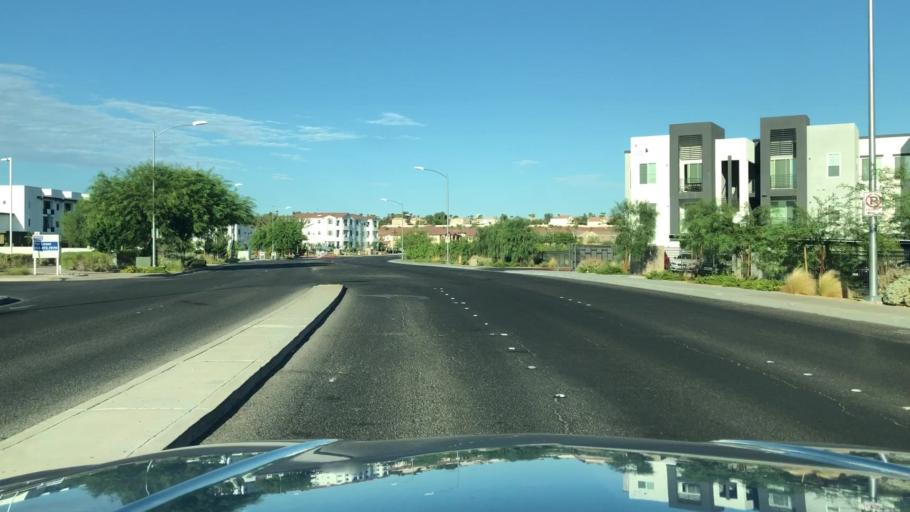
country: US
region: Nevada
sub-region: Clark County
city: Whitney
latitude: 36.0341
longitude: -115.0493
